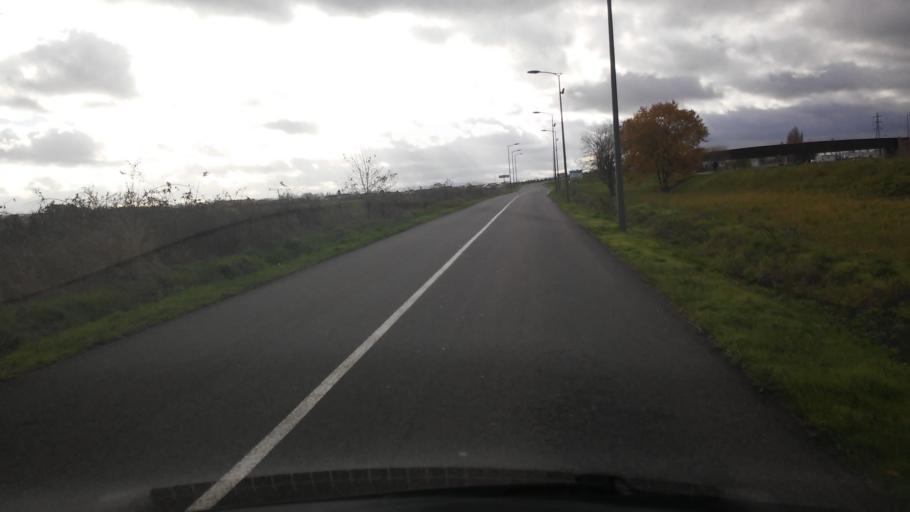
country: FR
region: Lorraine
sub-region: Departement de la Moselle
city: Talange
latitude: 49.2324
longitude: 6.1842
